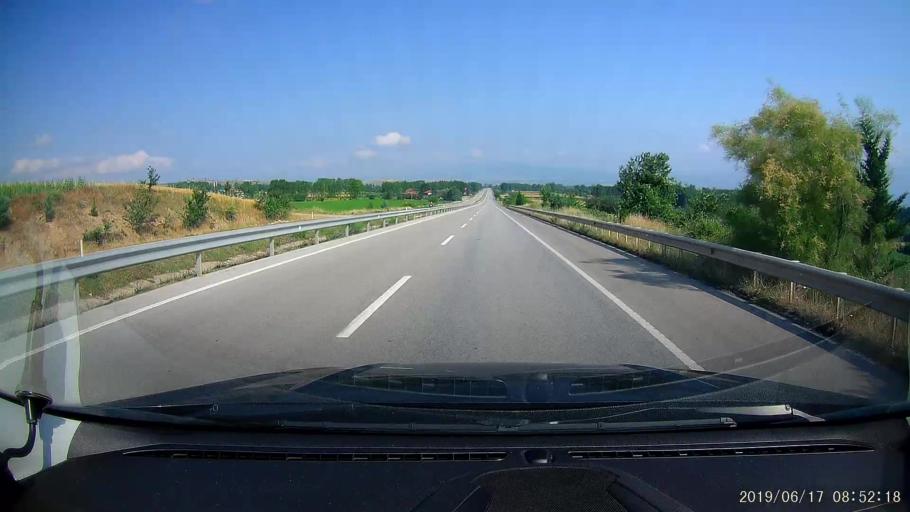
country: TR
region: Tokat
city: Erbaa
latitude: 40.6958
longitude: 36.4990
